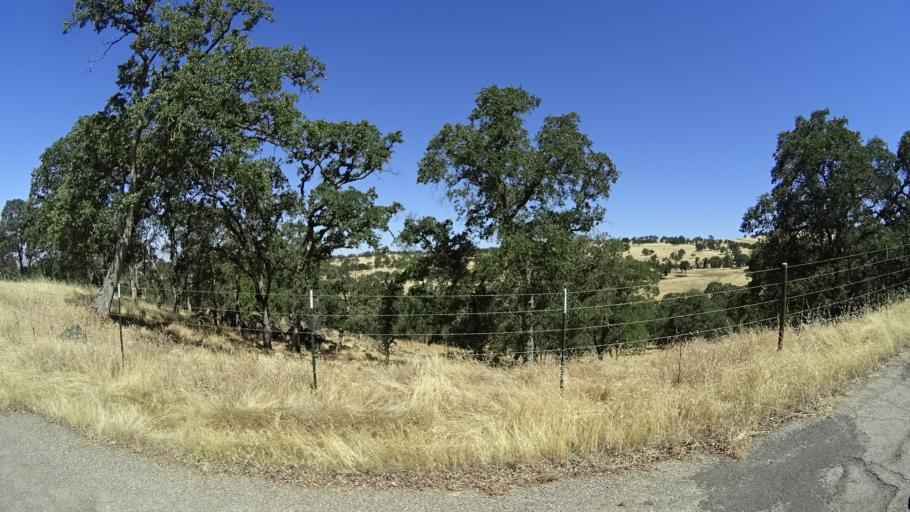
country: US
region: California
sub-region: Calaveras County
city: Copperopolis
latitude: 37.9398
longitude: -120.7328
